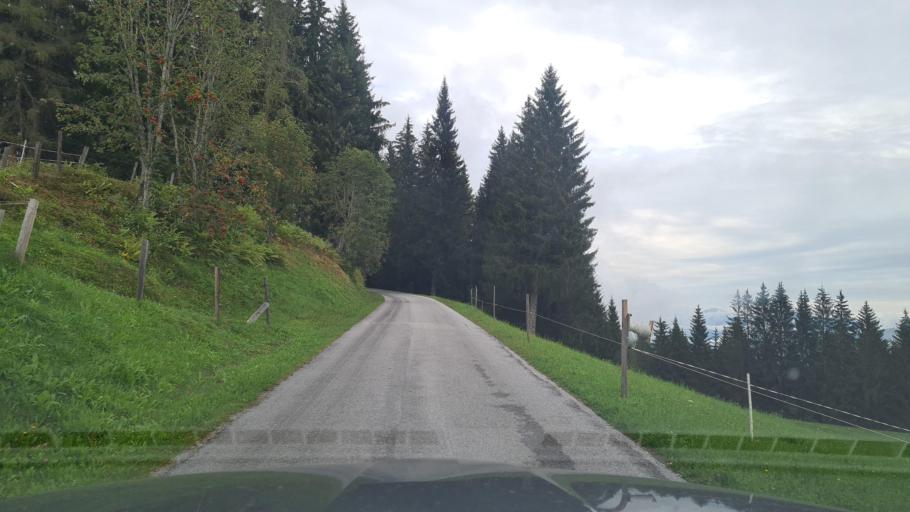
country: AT
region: Salzburg
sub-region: Politischer Bezirk Sankt Johann im Pongau
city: Sankt Johann im Pongau
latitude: 47.3570
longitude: 13.1799
